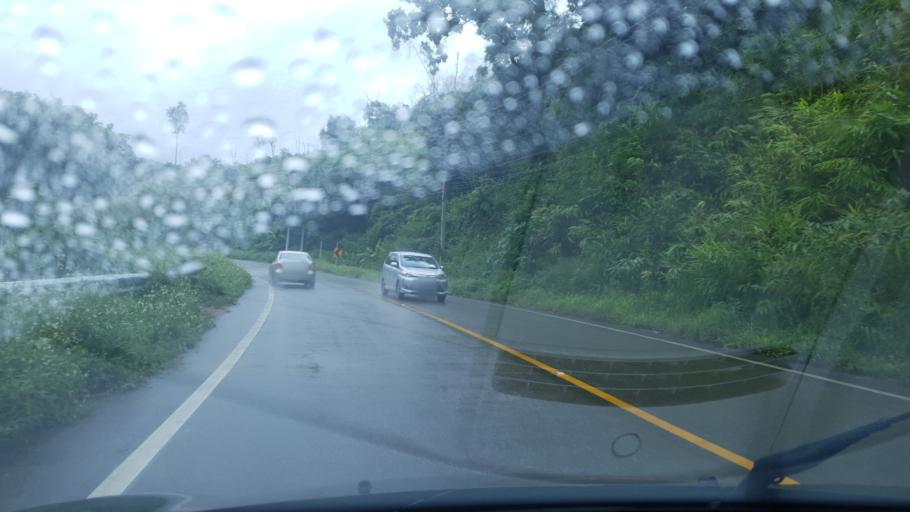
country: TH
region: Mae Hong Son
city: Khun Yuam
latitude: 18.6376
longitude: 97.9442
